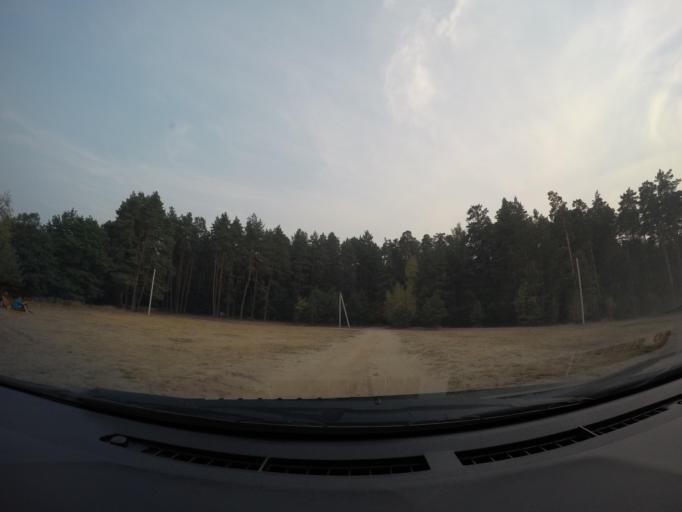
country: RU
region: Moskovskaya
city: Imeni Tsyurupy
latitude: 55.5065
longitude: 38.6936
